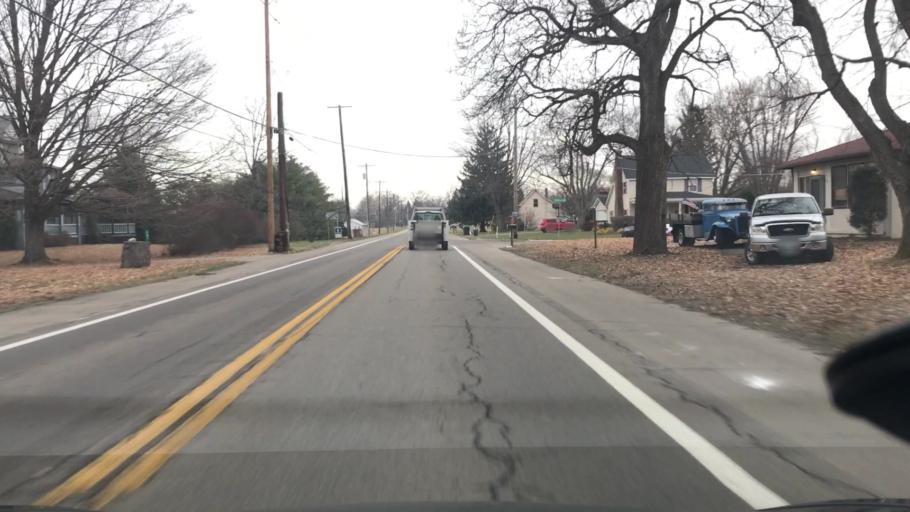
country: US
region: Ohio
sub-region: Madison County
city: London
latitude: 39.8947
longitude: -83.4586
